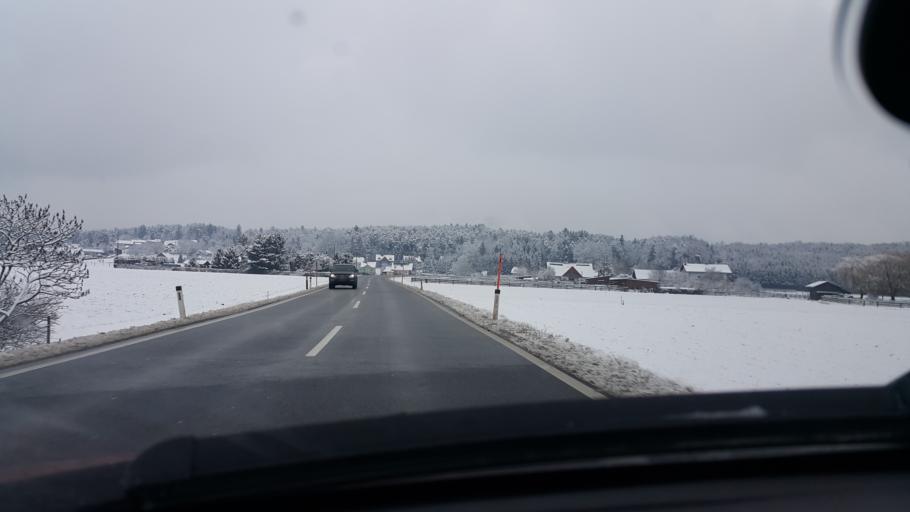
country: AT
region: Styria
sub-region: Politischer Bezirk Voitsberg
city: Mooskirchen
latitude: 47.0125
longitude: 15.2760
